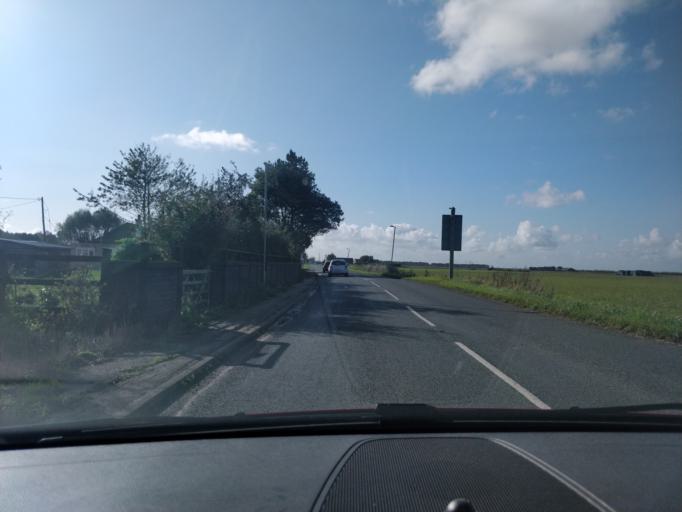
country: GB
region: England
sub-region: Lancashire
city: Banks
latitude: 53.6924
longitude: -2.9008
